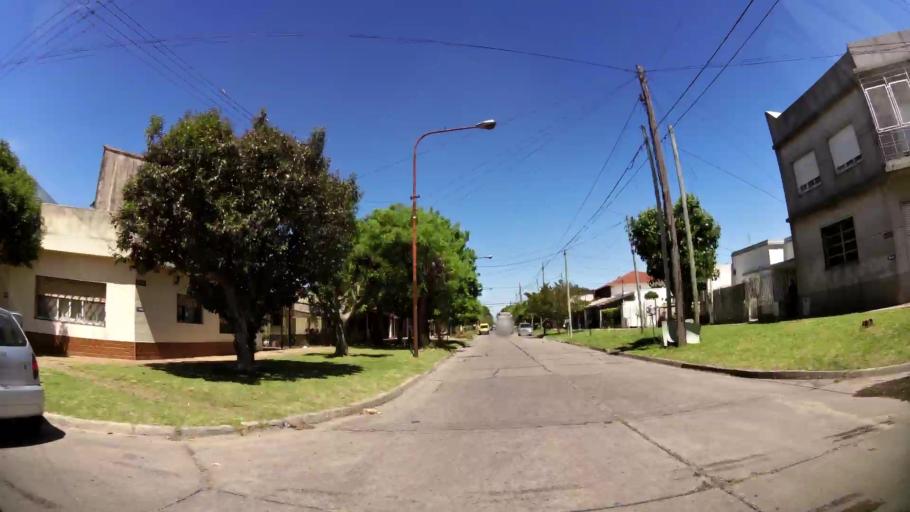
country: AR
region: Buenos Aires
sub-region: Partido de Quilmes
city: Quilmes
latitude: -34.7263
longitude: -58.2780
